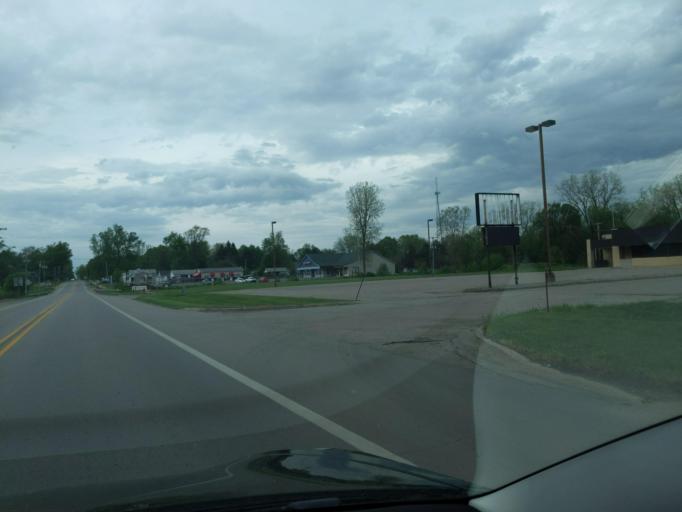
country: US
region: Michigan
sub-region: Ingham County
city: Stockbridge
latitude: 42.4405
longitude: -84.1801
